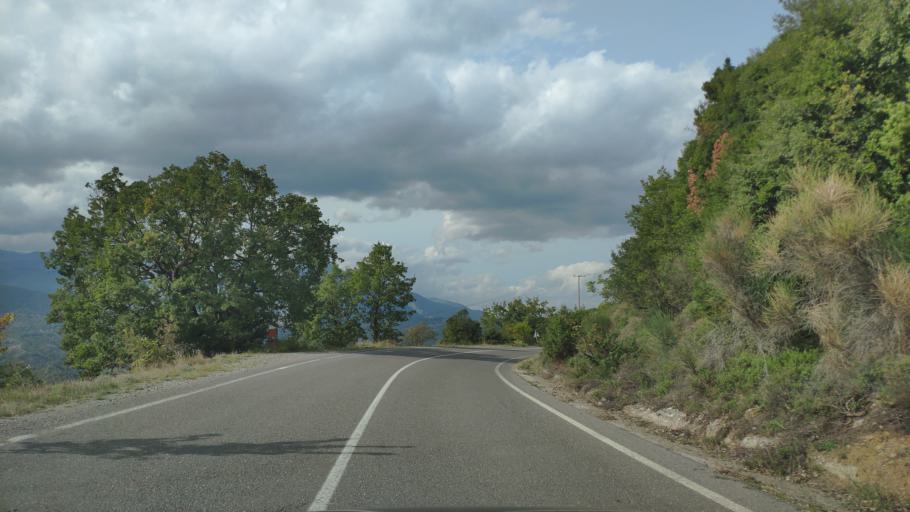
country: GR
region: Central Greece
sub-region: Nomos Fthiotidos
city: Anthili
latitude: 38.7403
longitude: 22.4466
